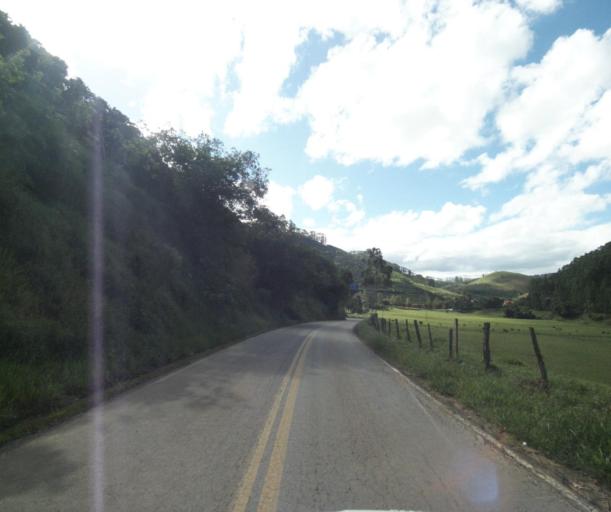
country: BR
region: Espirito Santo
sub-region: Irupi
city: Irupi
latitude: -20.5408
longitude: -41.6550
